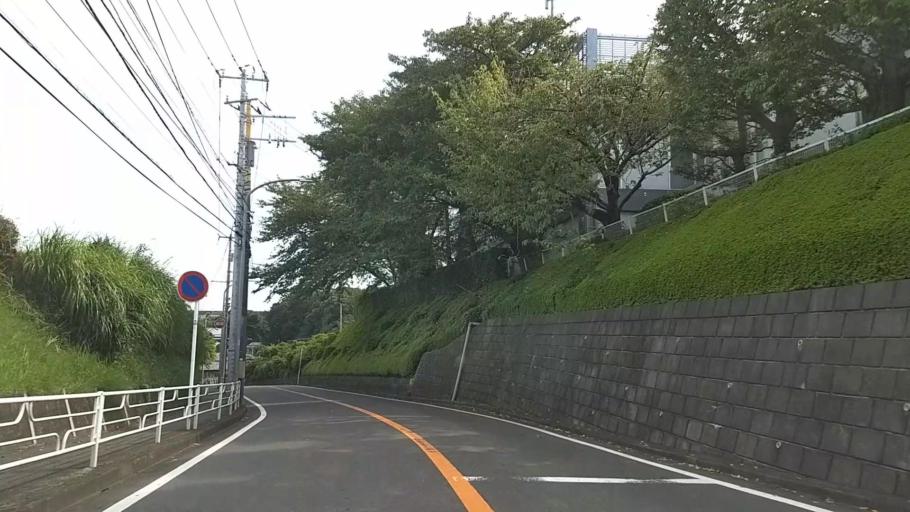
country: JP
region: Kanagawa
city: Yokohama
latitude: 35.4932
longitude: 139.5876
